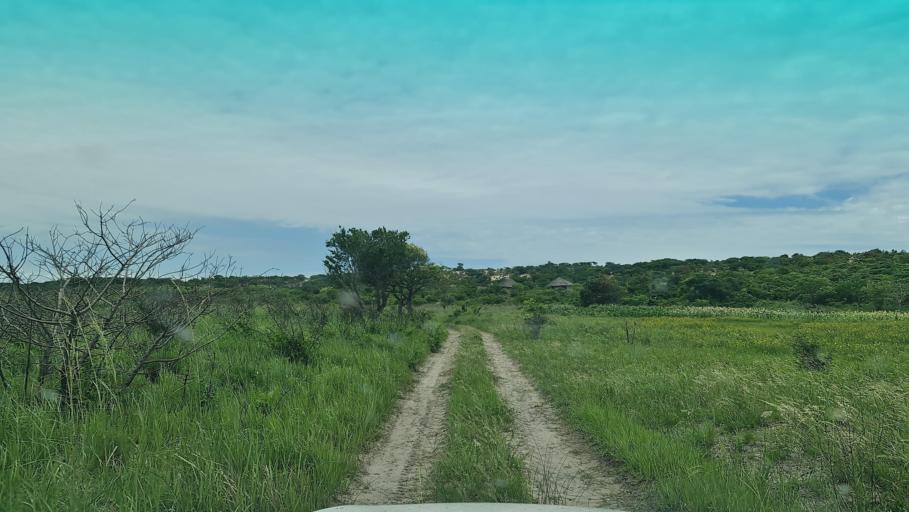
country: MZ
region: Maputo
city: Manhica
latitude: -25.6377
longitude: 32.7726
